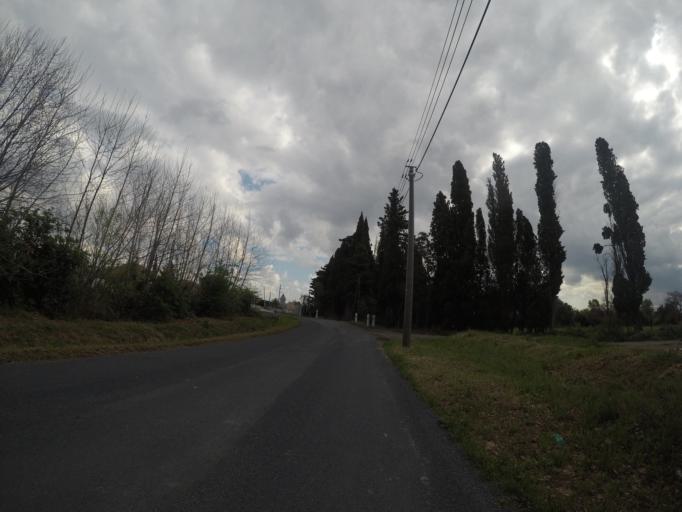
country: FR
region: Languedoc-Roussillon
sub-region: Departement des Pyrenees-Orientales
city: Le Soler
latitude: 42.6775
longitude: 2.7850
